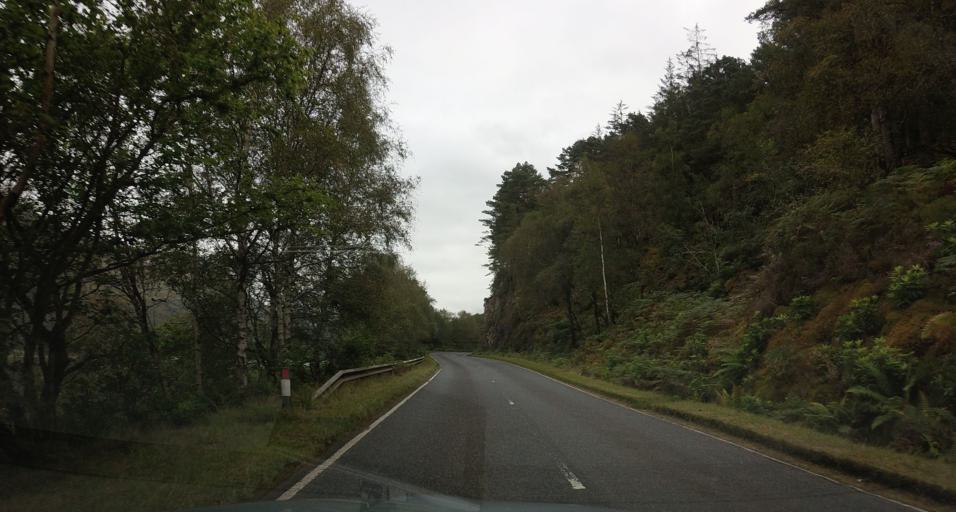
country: GB
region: Scotland
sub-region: Highland
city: Fort William
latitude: 56.6939
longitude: -5.0942
